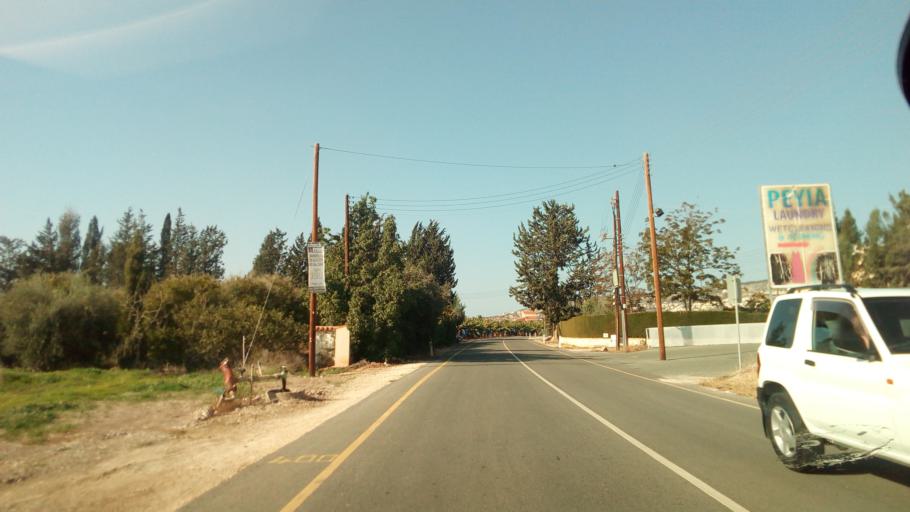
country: CY
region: Pafos
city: Pegeia
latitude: 34.8565
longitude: 32.3810
